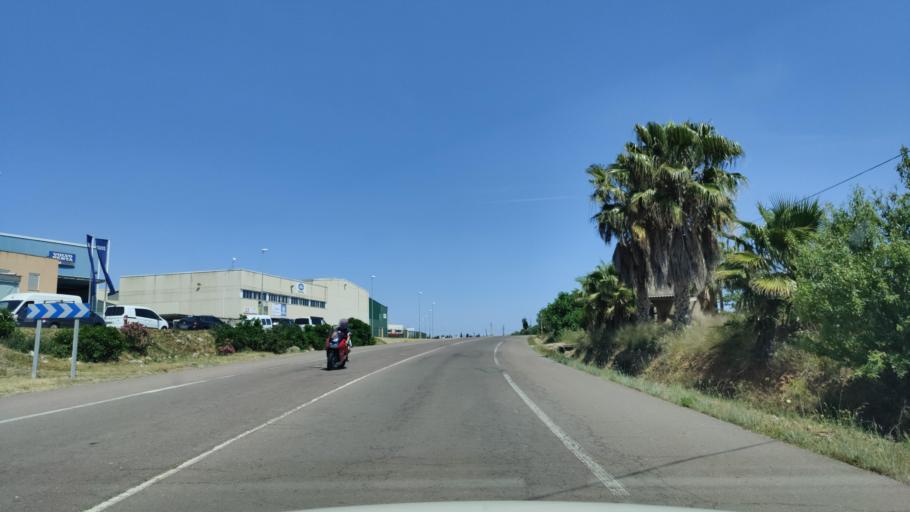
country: ES
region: Catalonia
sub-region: Provincia de Tarragona
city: Sant Carles de la Rapita
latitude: 40.6342
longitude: 0.5972
